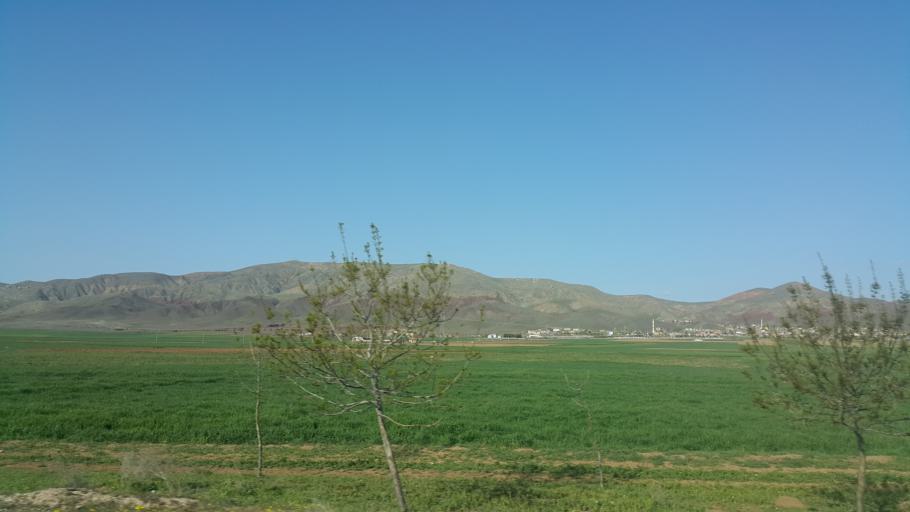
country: TR
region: Aksaray
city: Acipinar
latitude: 38.6133
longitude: 33.7620
